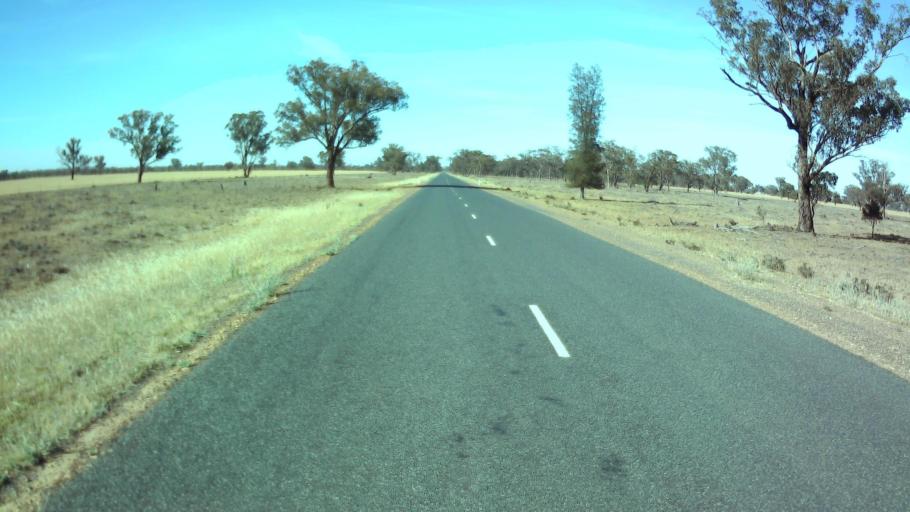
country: AU
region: New South Wales
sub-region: Weddin
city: Grenfell
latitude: -34.0837
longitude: 147.8941
